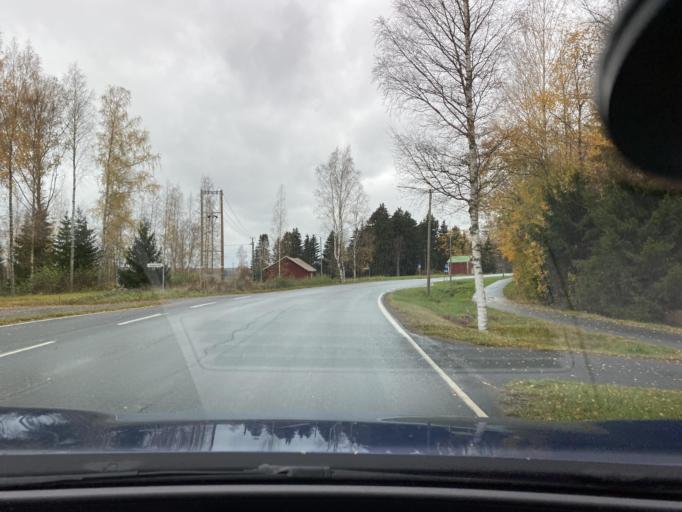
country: FI
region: Satakunta
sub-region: Pori
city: Kokemaeki
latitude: 61.2577
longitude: 22.3920
